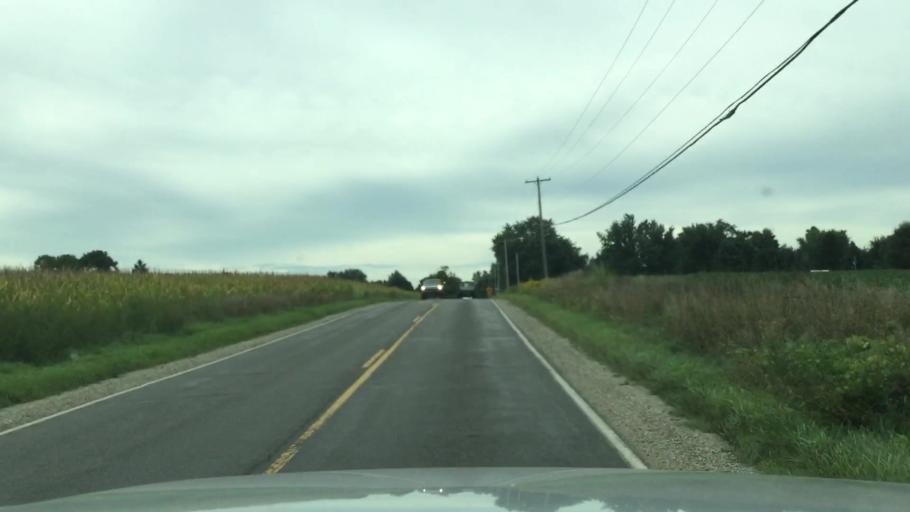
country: US
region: Michigan
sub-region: Shiawassee County
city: Durand
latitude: 42.9425
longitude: -83.9888
